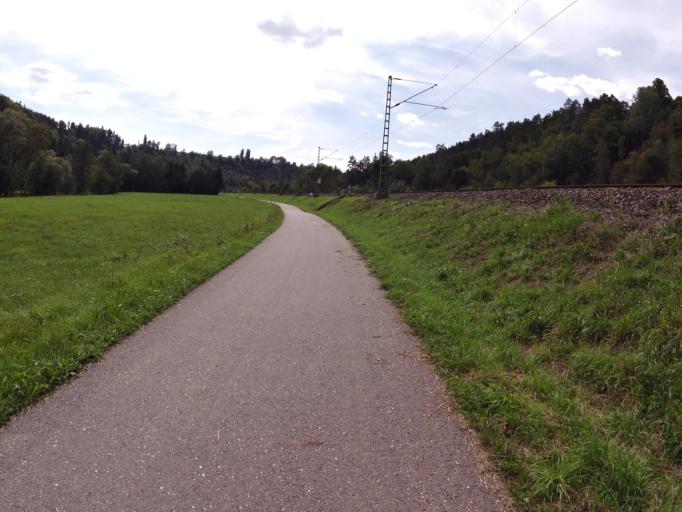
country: DE
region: Baden-Wuerttemberg
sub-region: Freiburg Region
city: Muhlheim am Bach
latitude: 48.3798
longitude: 8.6713
